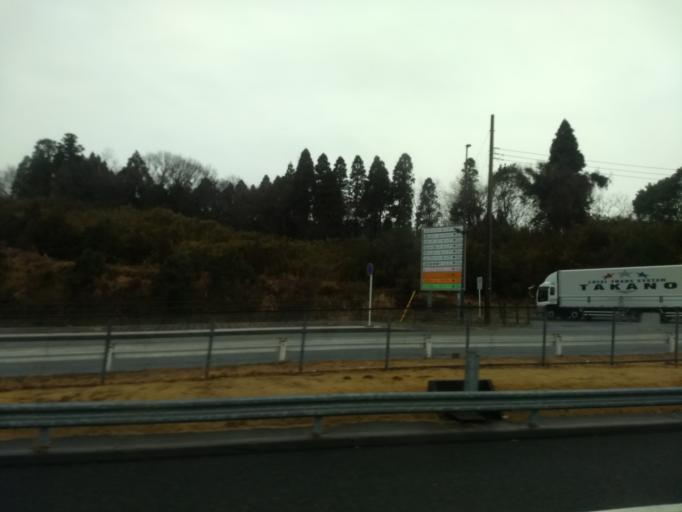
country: JP
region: Chiba
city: Narita
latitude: 35.7838
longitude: 140.3593
